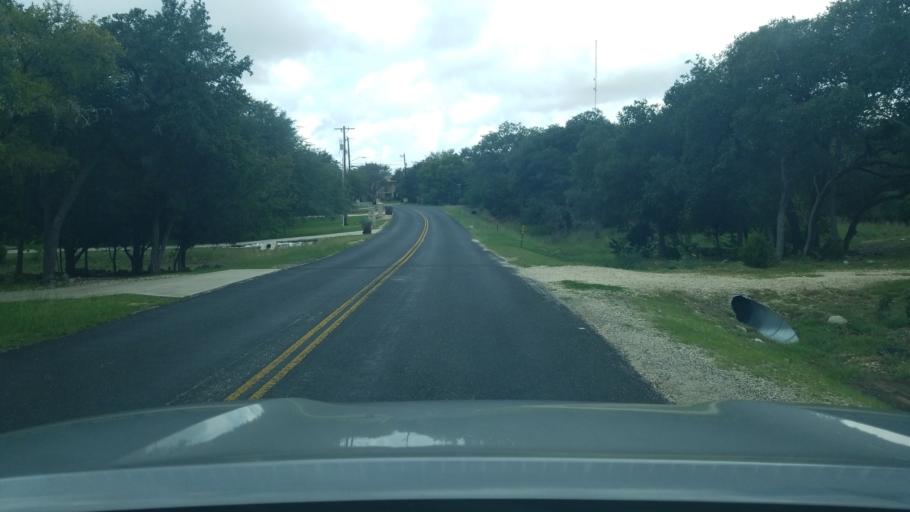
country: US
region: Texas
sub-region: Bexar County
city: Timberwood Park
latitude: 29.6934
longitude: -98.5044
